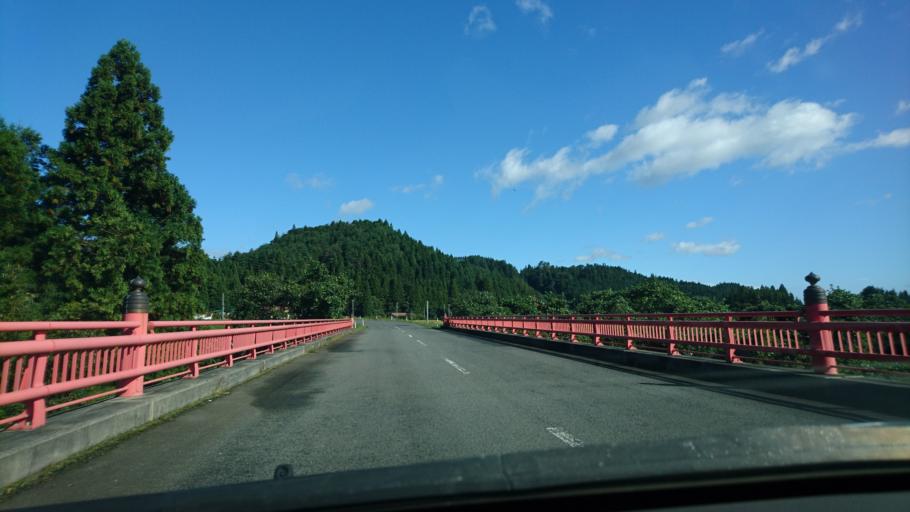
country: JP
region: Iwate
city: Ichinoseki
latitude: 39.0113
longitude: 141.0276
